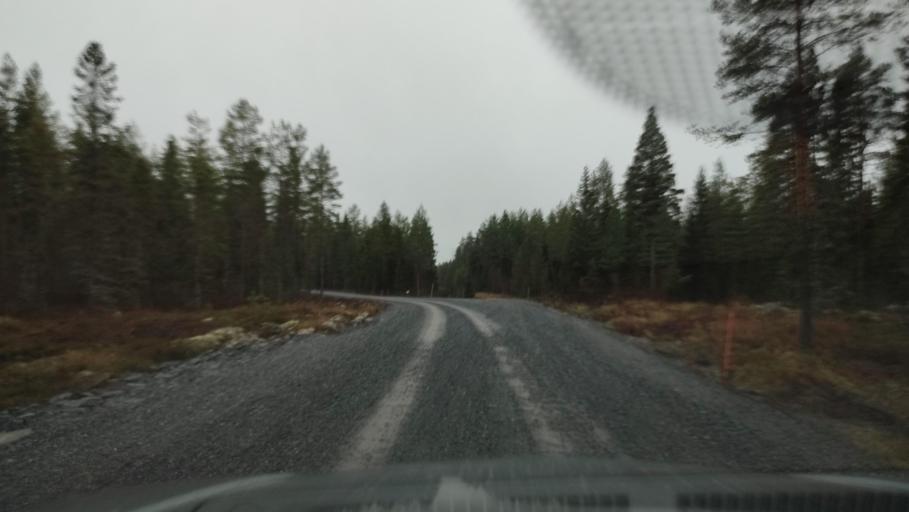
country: FI
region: Southern Ostrobothnia
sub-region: Suupohja
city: Karijoki
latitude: 62.1609
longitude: 21.5899
